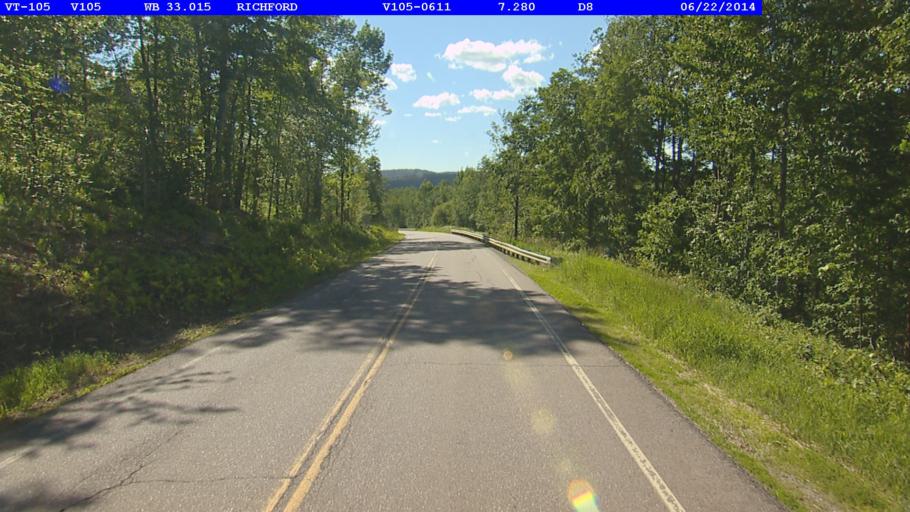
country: US
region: Vermont
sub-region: Franklin County
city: Richford
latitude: 45.0037
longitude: -72.5785
